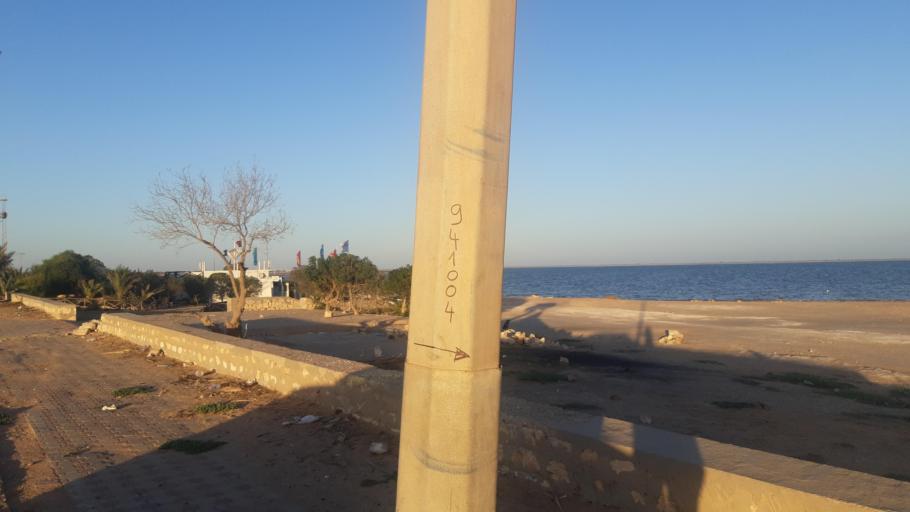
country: TN
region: Madanin
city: Midoun
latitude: 33.7224
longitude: 10.9516
